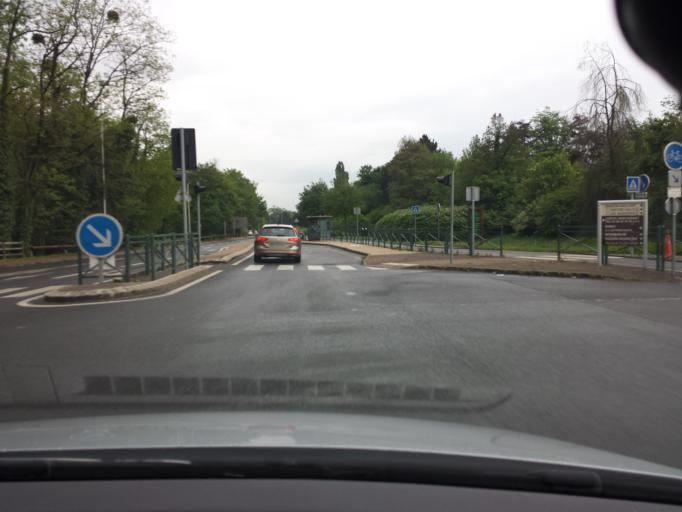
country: FR
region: Ile-de-France
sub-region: Departement de l'Essonne
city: Verrieres-le-Buisson
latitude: 48.7546
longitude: 2.2744
